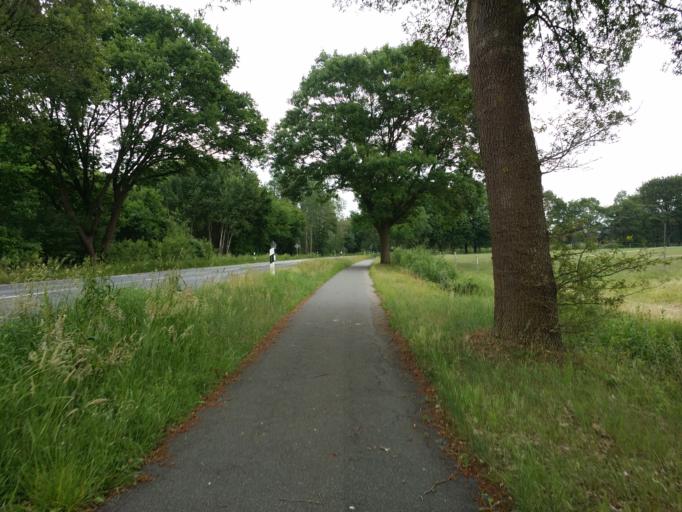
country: DE
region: Lower Saxony
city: Hatten
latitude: 53.0847
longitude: 8.3823
